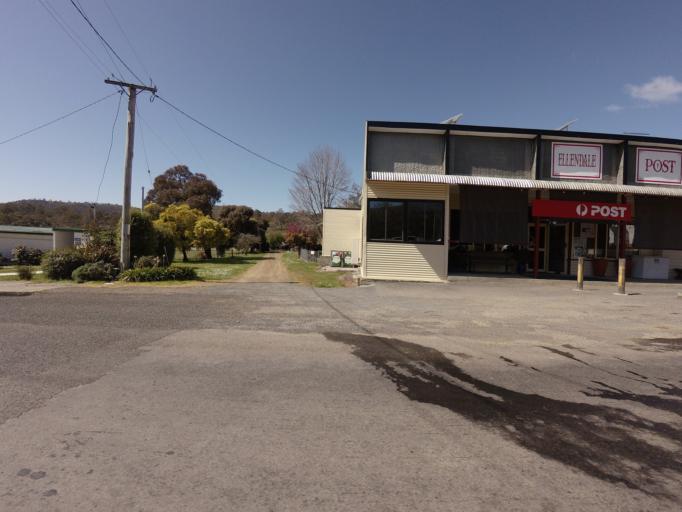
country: AU
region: Tasmania
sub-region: Derwent Valley
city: New Norfolk
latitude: -42.6185
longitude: 146.7165
